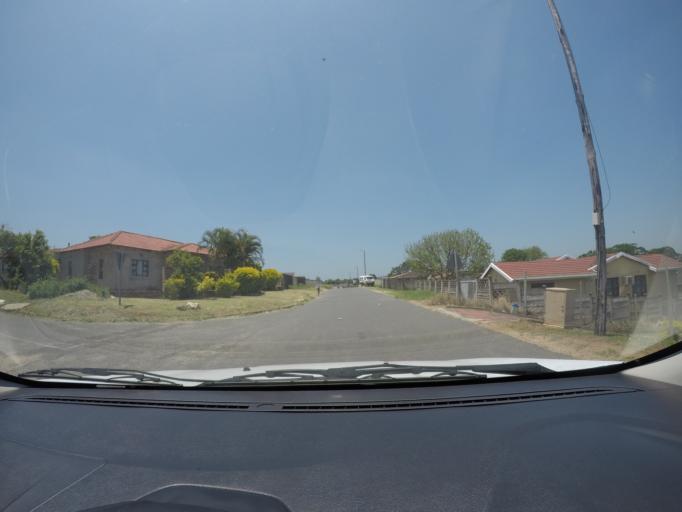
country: ZA
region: KwaZulu-Natal
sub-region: uThungulu District Municipality
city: eSikhawini
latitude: -28.8759
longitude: 31.9072
